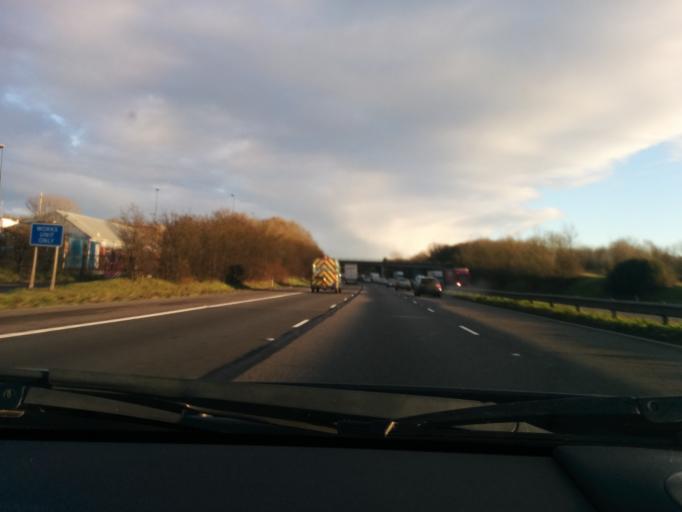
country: GB
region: England
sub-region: Oxfordshire
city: Chalgrove
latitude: 51.7258
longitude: -1.0603
